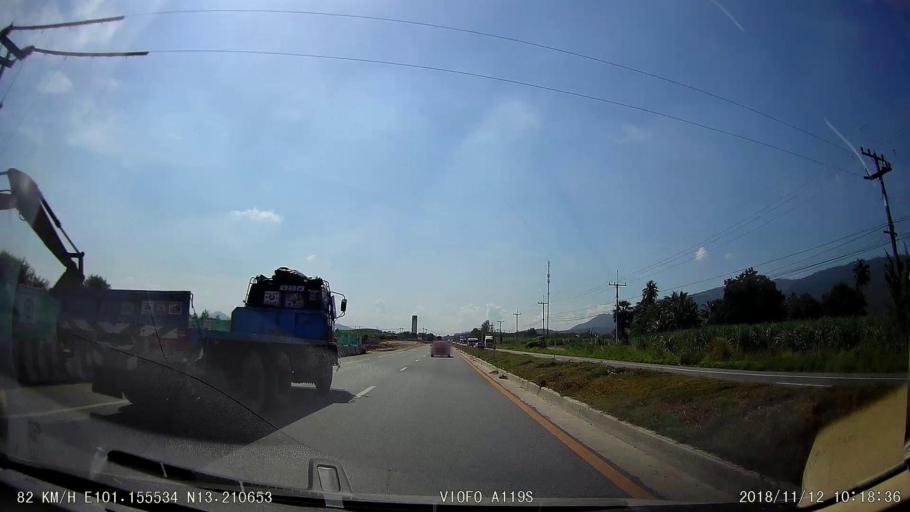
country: TH
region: Chon Buri
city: Ban Bueng
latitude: 13.2101
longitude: 101.1556
